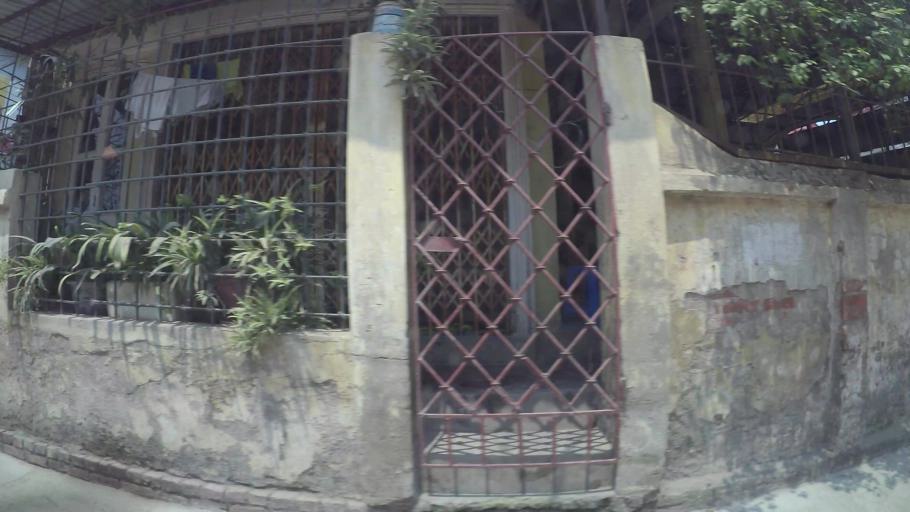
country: VN
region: Ha Noi
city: Van Dien
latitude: 20.9507
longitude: 105.8305
